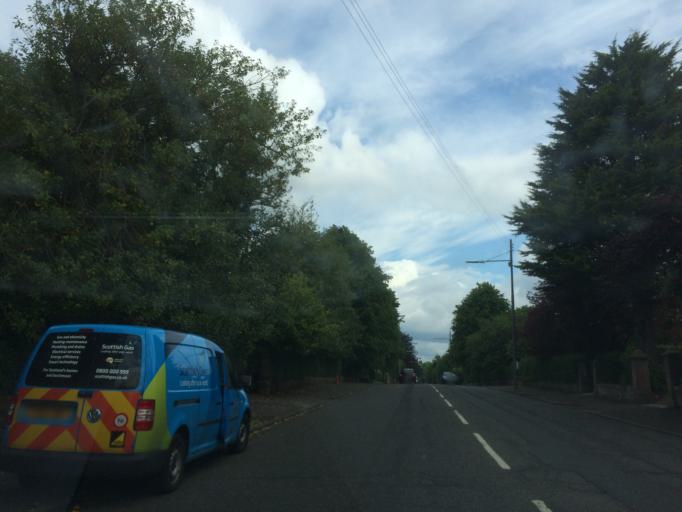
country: GB
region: Scotland
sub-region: East Renfrewshire
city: Giffnock
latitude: 55.8144
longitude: -4.2781
